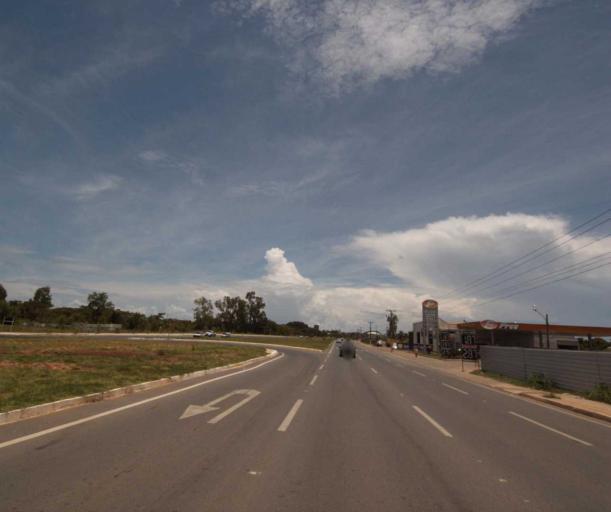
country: BR
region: Mato Grosso
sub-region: Varzea Grande
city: Varzea Grande
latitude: -15.6091
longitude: -56.1434
